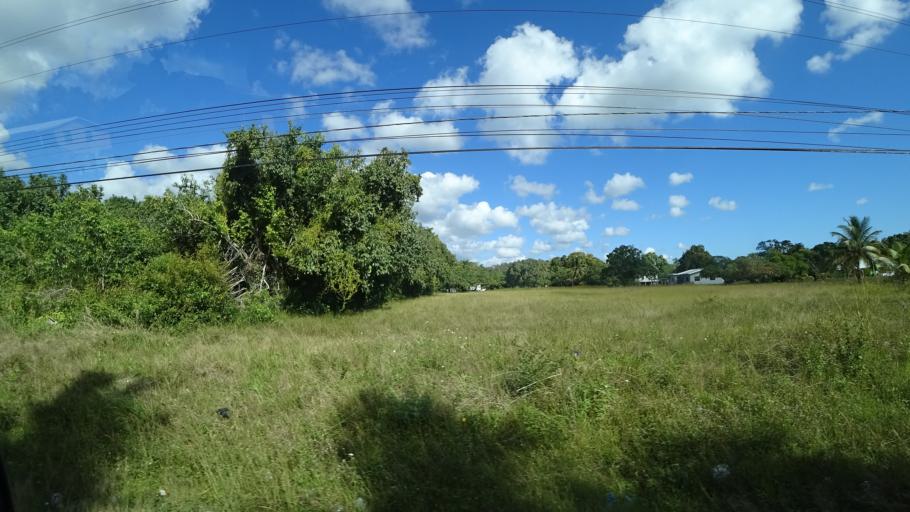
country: BZ
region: Belize
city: Belize City
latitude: 17.5692
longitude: -88.4043
